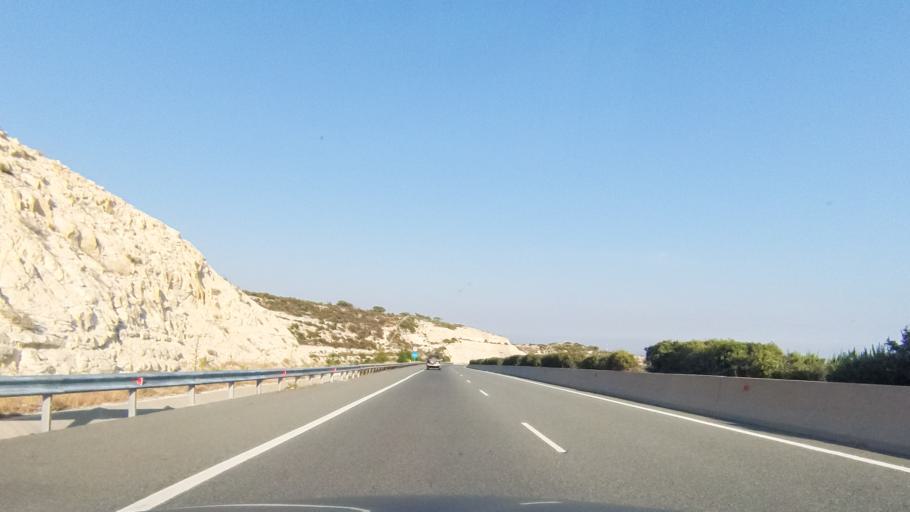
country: CY
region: Limassol
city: Sotira
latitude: 34.6927
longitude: 32.8664
